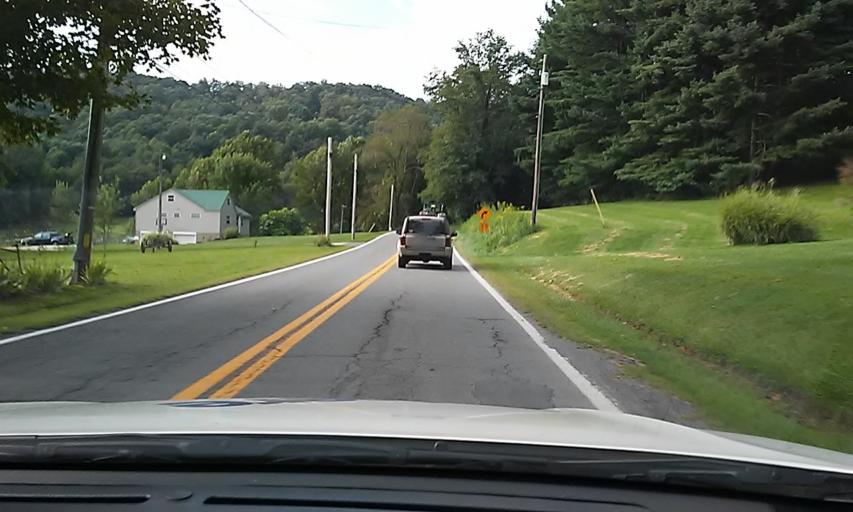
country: US
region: West Virginia
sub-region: Marion County
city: Mannington
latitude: 39.6930
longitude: -80.3164
